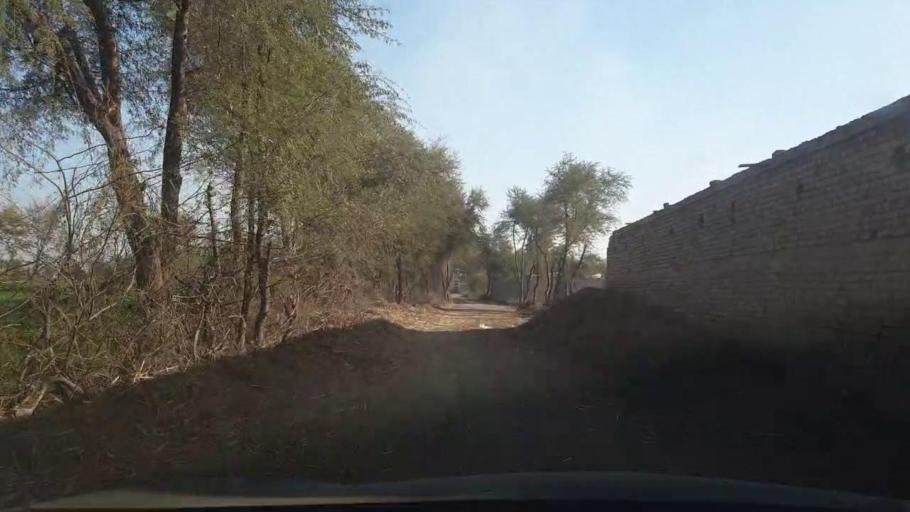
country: PK
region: Sindh
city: Ghotki
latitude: 28.0750
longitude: 69.3750
